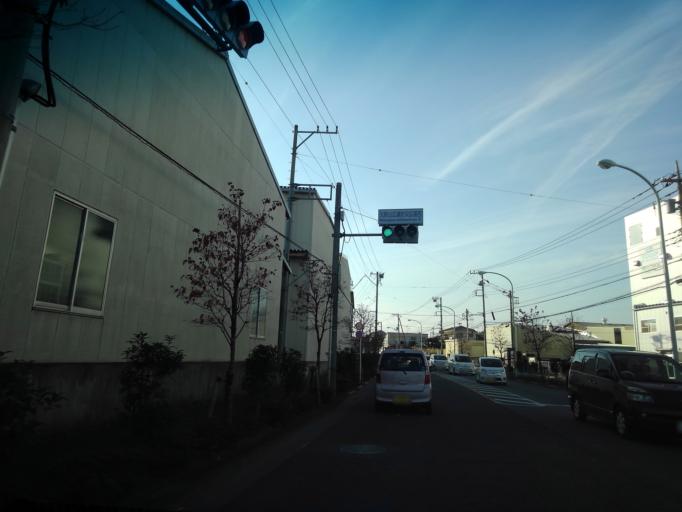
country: JP
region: Tokyo
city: Fussa
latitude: 35.7932
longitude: 139.3494
